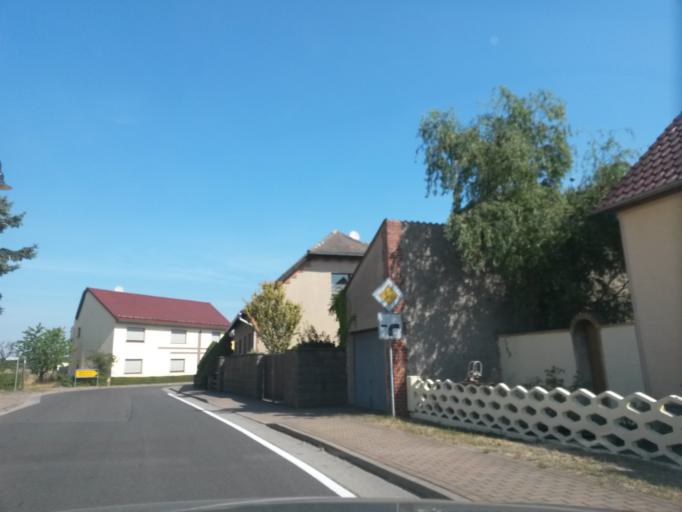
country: DE
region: Brandenburg
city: Wiesenburg
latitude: 52.0574
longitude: 12.3814
